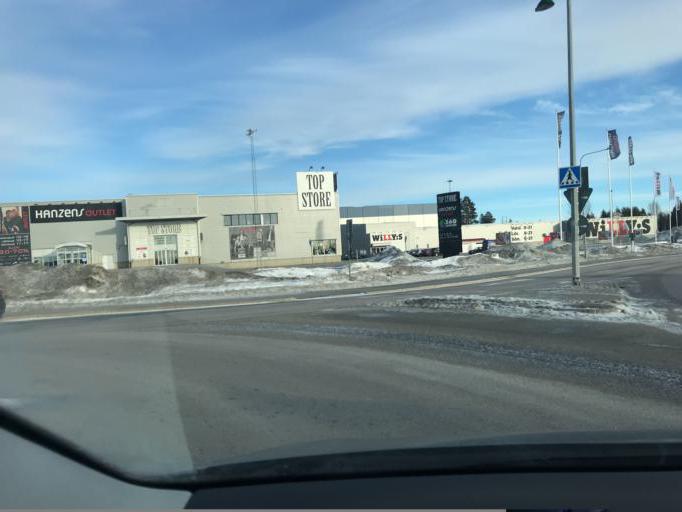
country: SE
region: Norrbotten
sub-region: Lulea Kommun
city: Gammelstad
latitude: 65.6190
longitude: 22.0519
